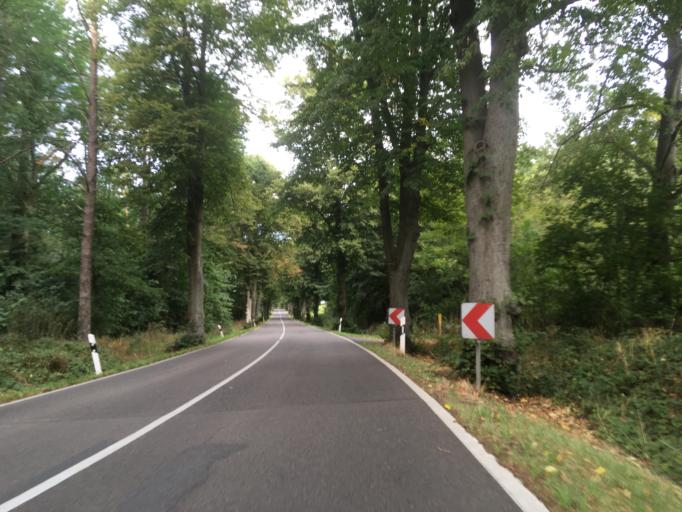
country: DE
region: Brandenburg
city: Templin
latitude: 53.1903
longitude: 13.5641
